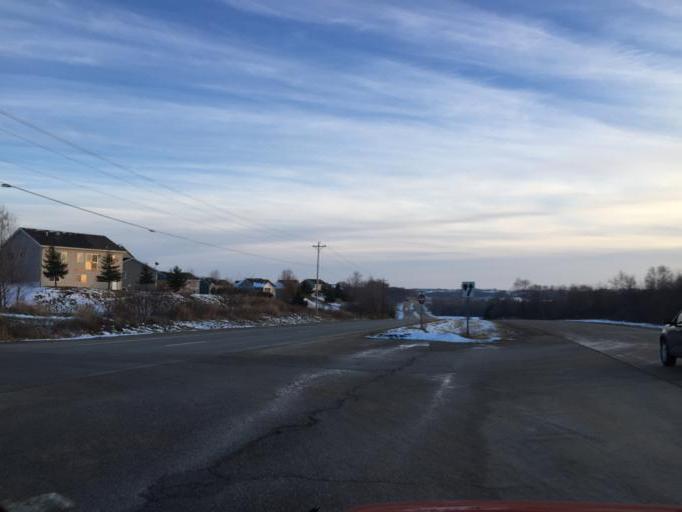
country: US
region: Minnesota
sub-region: Olmsted County
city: Rochester
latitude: 44.0372
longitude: -92.4266
